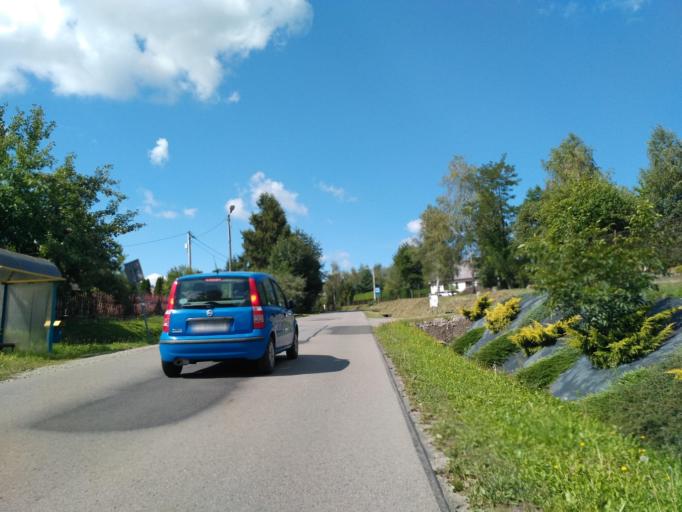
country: PL
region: Subcarpathian Voivodeship
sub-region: Powiat jasielski
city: Brzyska
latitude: 49.7809
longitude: 21.3764
